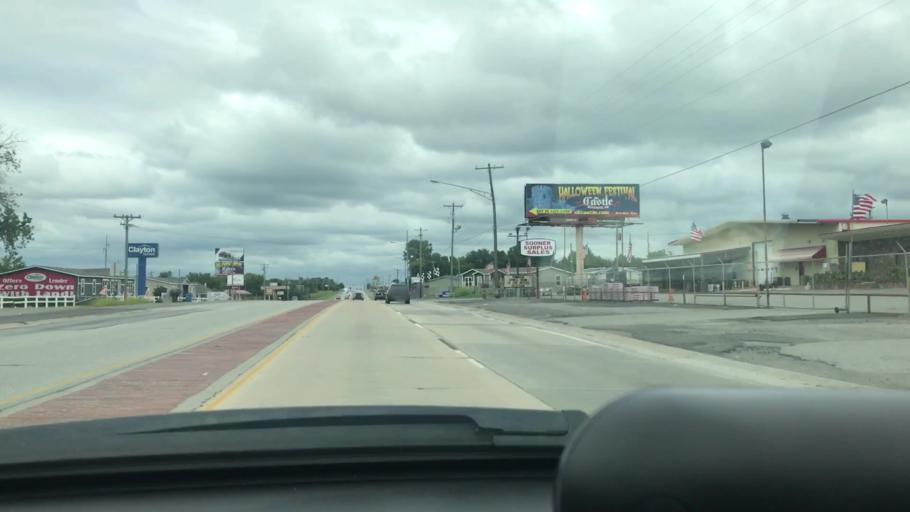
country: US
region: Oklahoma
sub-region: Muskogee County
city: Muskogee
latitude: 35.7741
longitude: -95.4025
